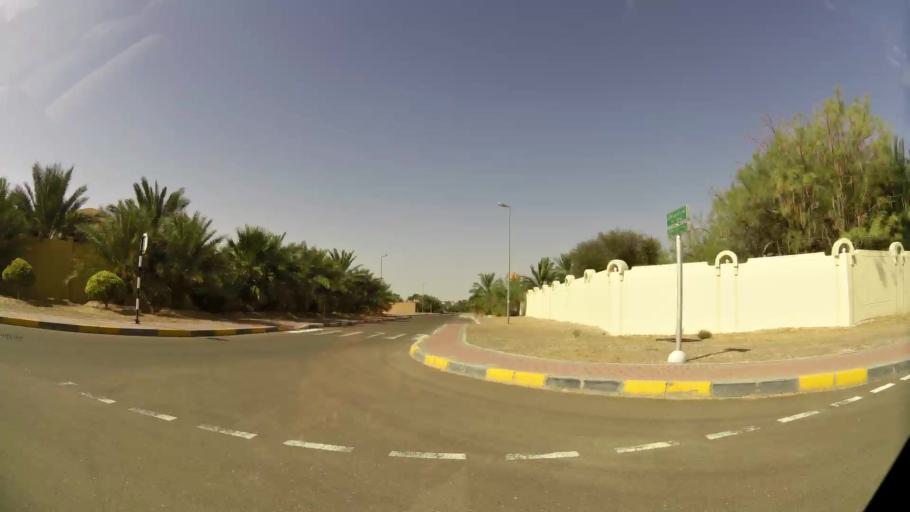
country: OM
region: Al Buraimi
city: Al Buraymi
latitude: 24.3171
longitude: 55.8081
